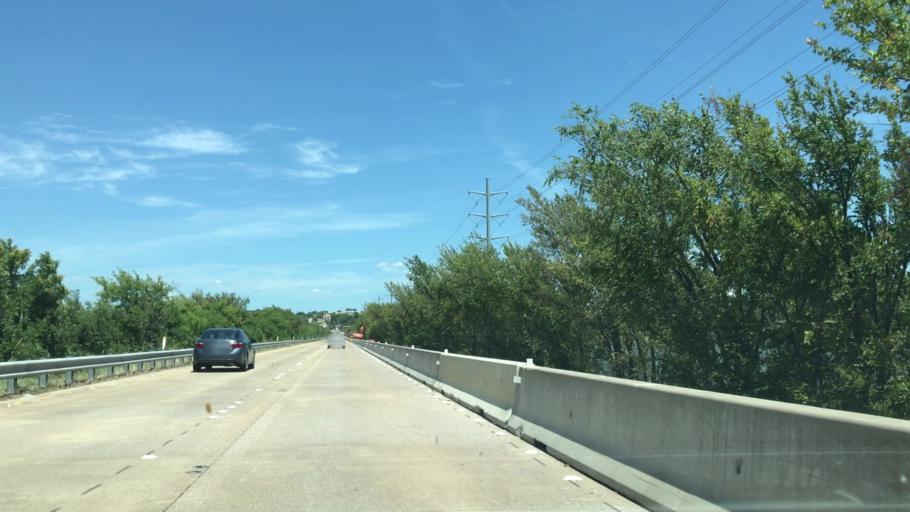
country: US
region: Texas
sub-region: Rockwall County
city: Rockwall
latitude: 32.9270
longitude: -96.4806
